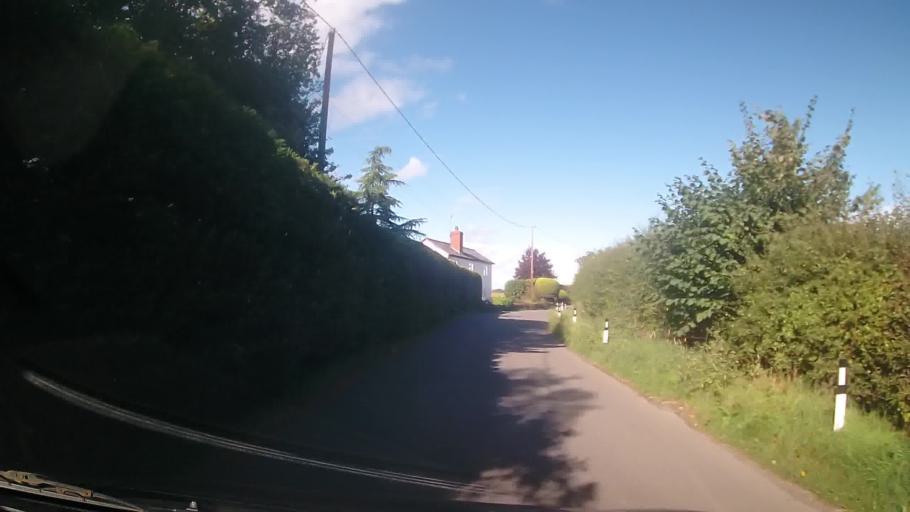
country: GB
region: England
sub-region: Shropshire
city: Wem
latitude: 52.8506
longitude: -2.7025
